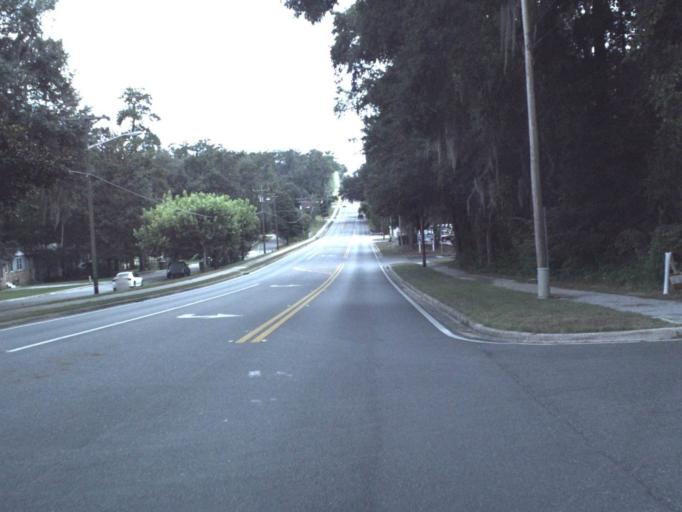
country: US
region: Florida
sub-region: Columbia County
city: Lake City
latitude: 30.1714
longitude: -82.6374
